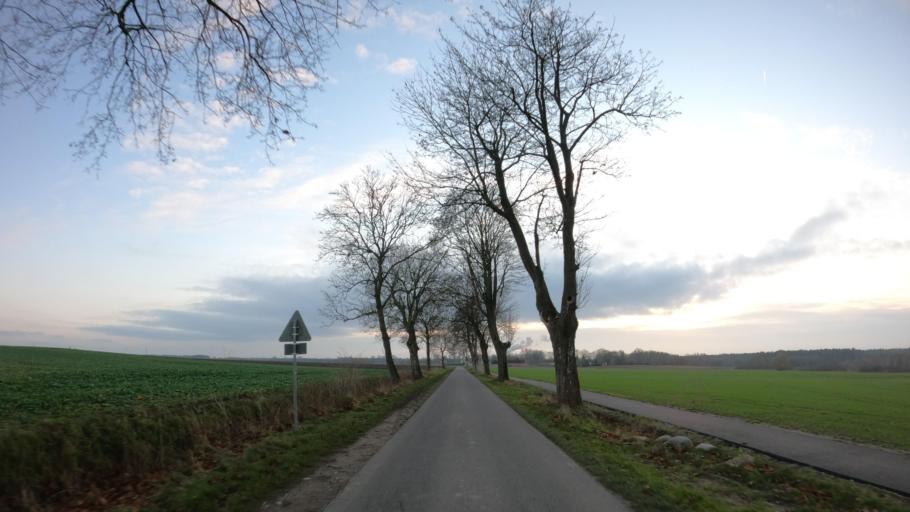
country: PL
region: West Pomeranian Voivodeship
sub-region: Powiat bialogardzki
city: Karlino
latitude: 54.0876
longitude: 15.8848
